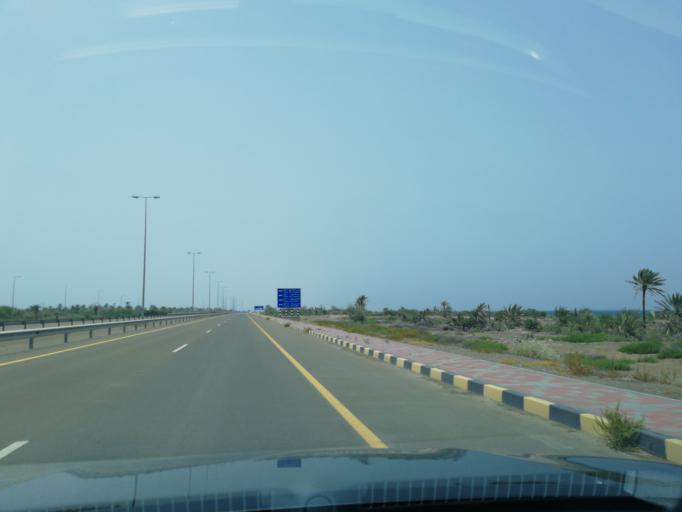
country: OM
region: Al Batinah
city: Al Liwa'
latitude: 24.6345
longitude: 56.5251
